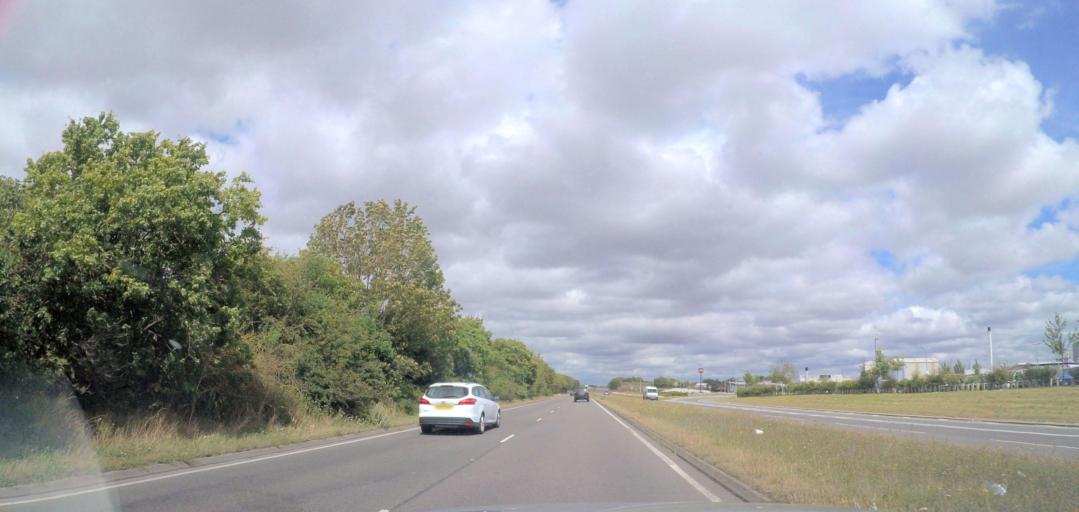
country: GB
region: England
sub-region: Hertfordshire
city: Royston
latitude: 52.0556
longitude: -0.0410
